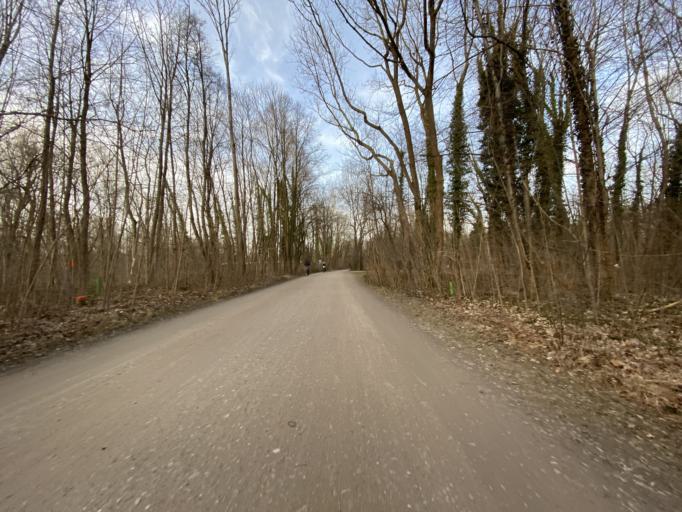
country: DE
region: Bavaria
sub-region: Upper Bavaria
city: Unterfoehring
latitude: 48.1769
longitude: 11.6248
